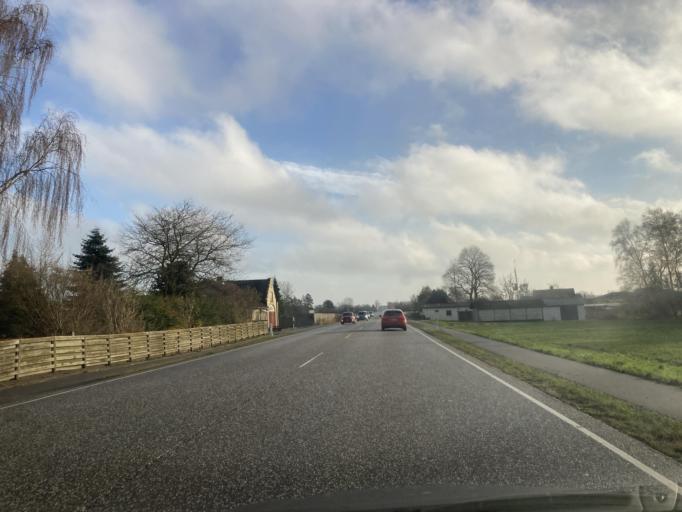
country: DK
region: Zealand
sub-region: Guldborgsund Kommune
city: Sundby
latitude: 54.7744
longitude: 11.7368
